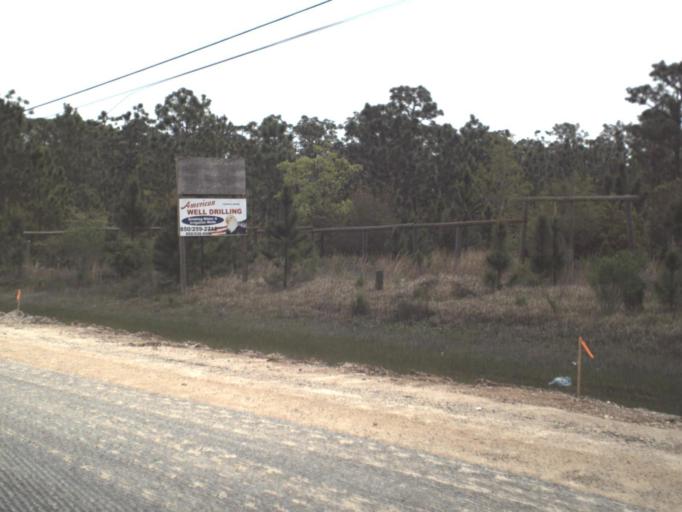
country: US
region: Florida
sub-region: Santa Rosa County
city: Woodlawn Beach
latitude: 30.4038
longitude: -86.9658
